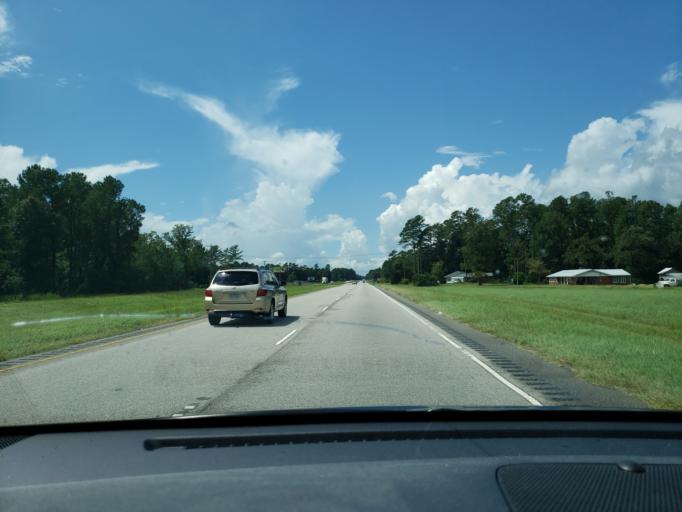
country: US
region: North Carolina
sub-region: Bladen County
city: Elizabethtown
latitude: 34.6455
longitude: -78.6908
